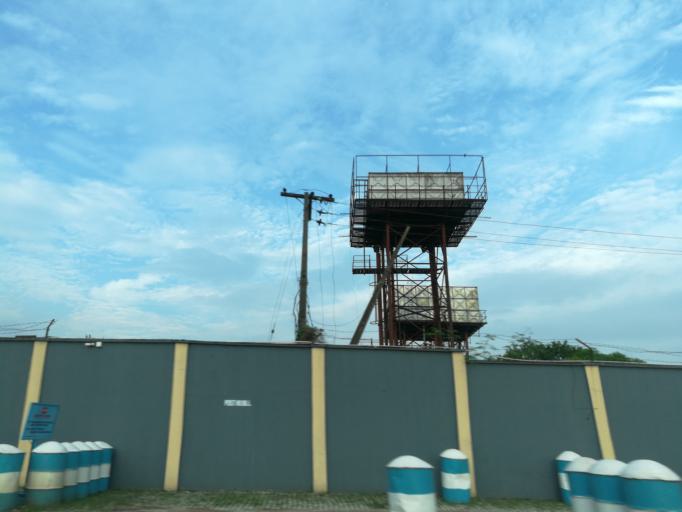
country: NG
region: Lagos
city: Oshodi
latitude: 6.5741
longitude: 3.3341
